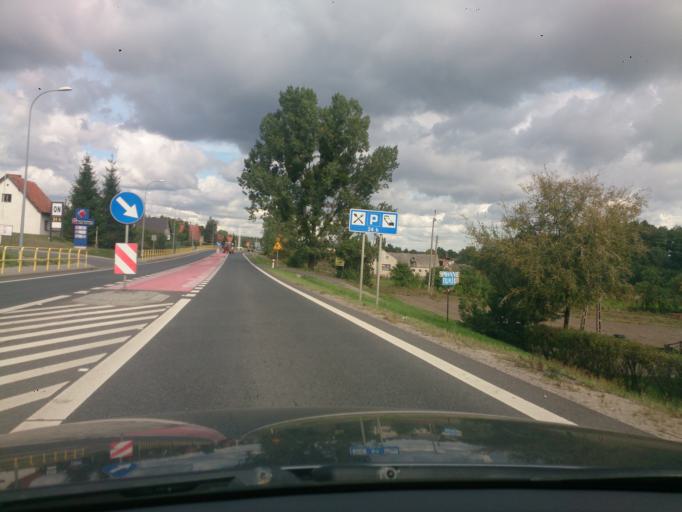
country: PL
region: Kujawsko-Pomorskie
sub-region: Grudziadz
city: Grudziadz
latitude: 53.4941
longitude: 18.6788
